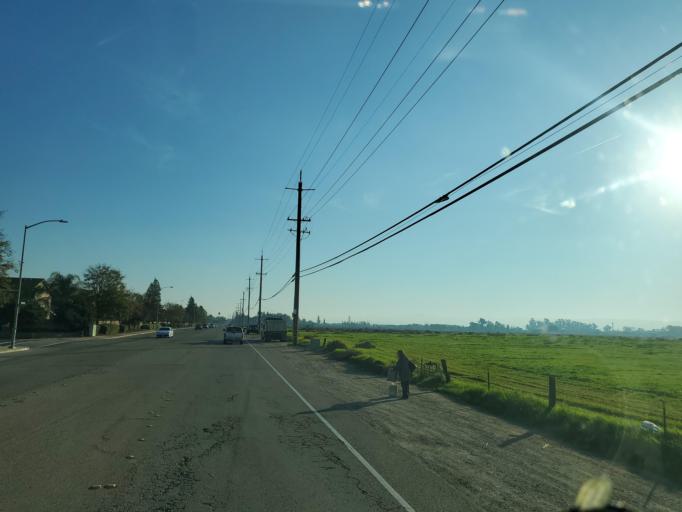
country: US
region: California
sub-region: San Joaquin County
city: Lathrop
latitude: 37.8088
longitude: -121.2529
